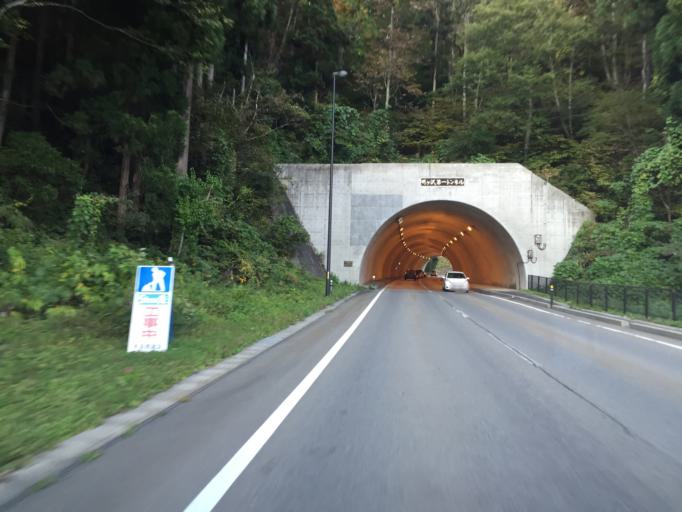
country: JP
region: Fukushima
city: Kitakata
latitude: 37.7442
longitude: 139.8864
